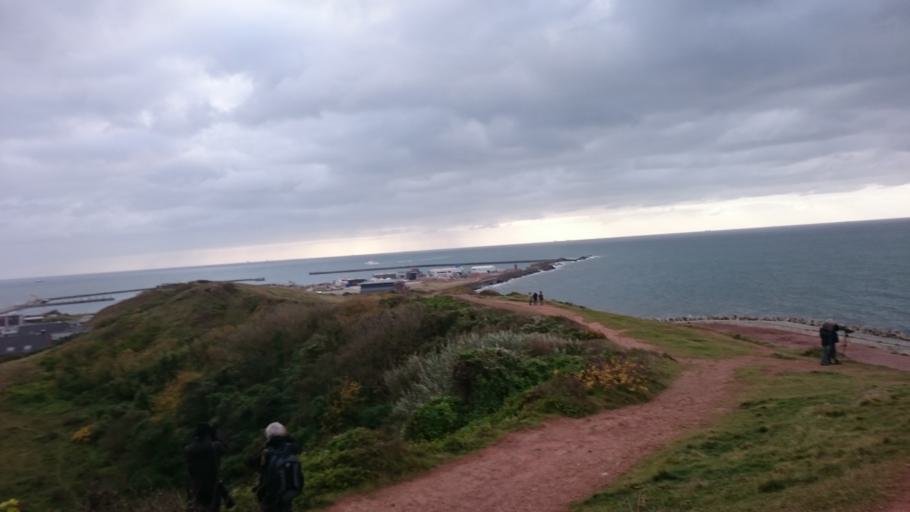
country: DE
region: Schleswig-Holstein
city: Helgoland
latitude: 54.1797
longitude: 7.8835
